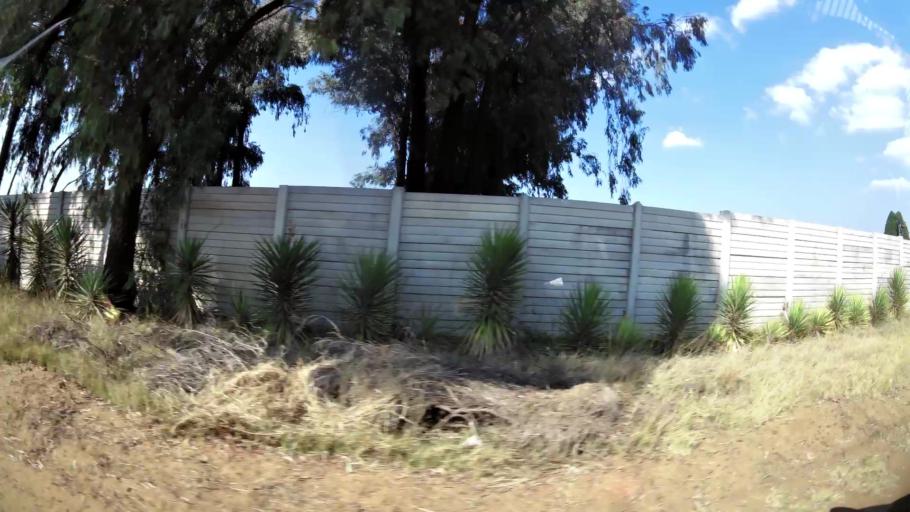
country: ZA
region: Gauteng
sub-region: Ekurhuleni Metropolitan Municipality
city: Benoni
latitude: -26.0785
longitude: 28.3520
